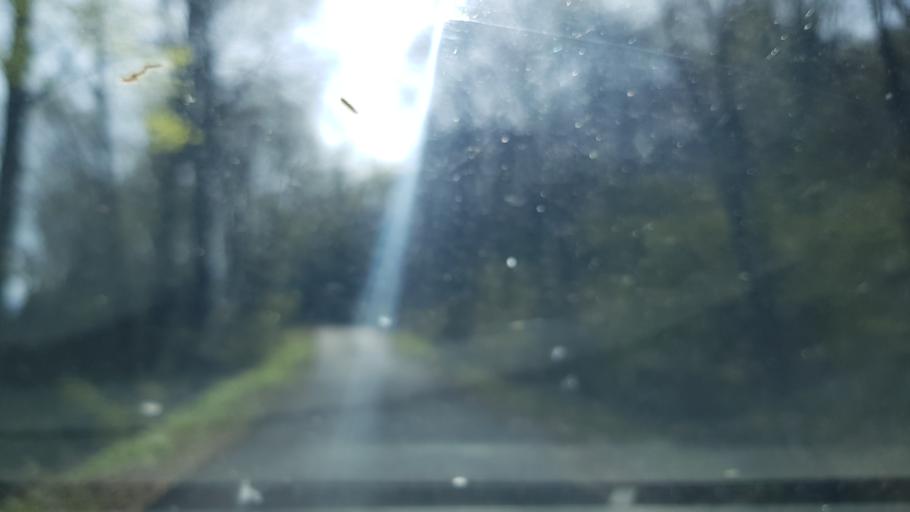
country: IT
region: Friuli Venezia Giulia
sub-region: Provincia di Udine
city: Trasaghis
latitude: 46.2875
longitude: 13.0316
